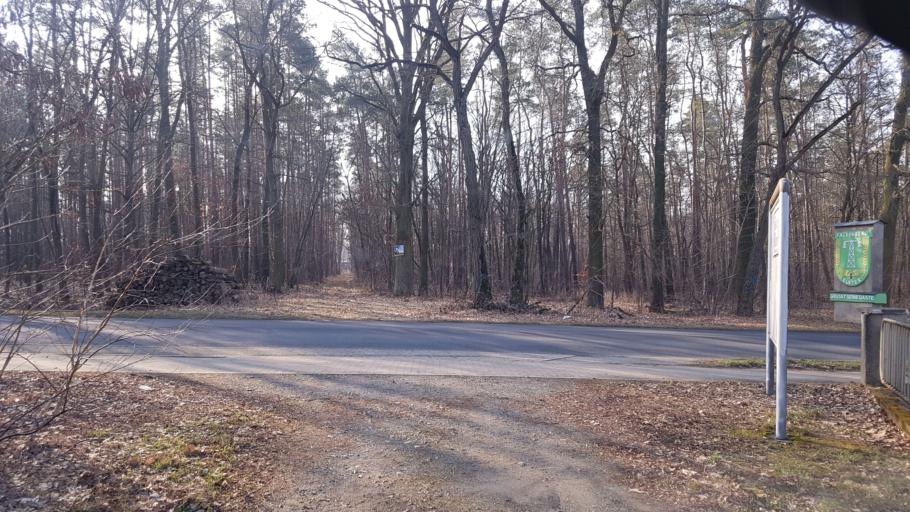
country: DE
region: Brandenburg
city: Falkenberg
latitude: 51.5881
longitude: 13.2713
